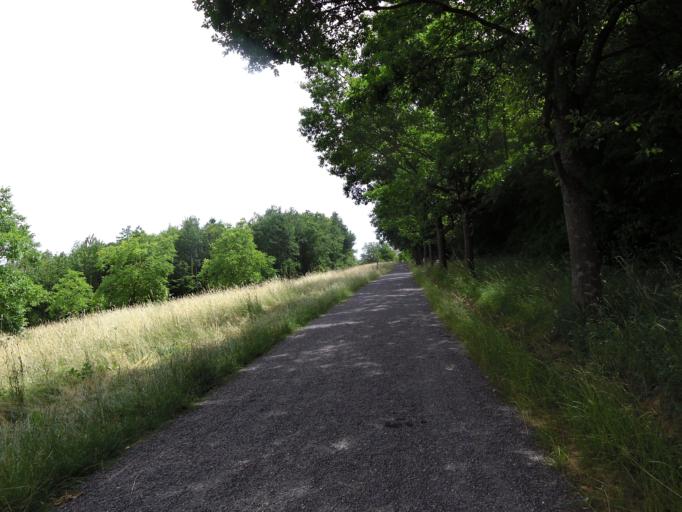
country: DE
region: Bavaria
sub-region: Regierungsbezirk Unterfranken
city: Gerbrunn
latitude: 49.7936
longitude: 9.9788
